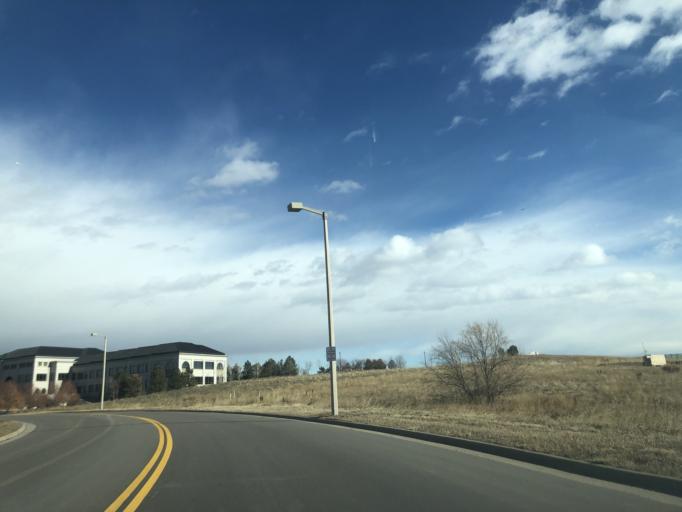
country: US
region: Colorado
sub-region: Douglas County
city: Meridian
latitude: 39.5515
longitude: -104.8476
